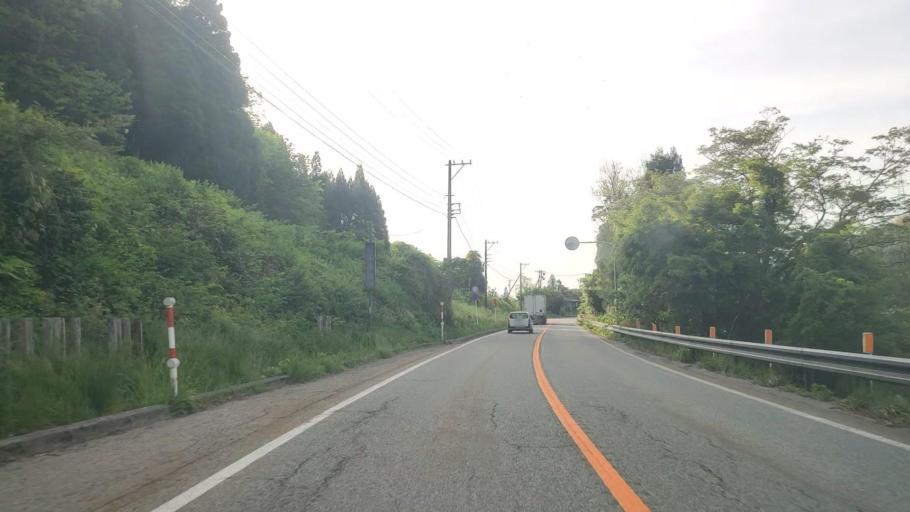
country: JP
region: Toyama
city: Yatsuomachi-higashikumisaka
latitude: 36.5534
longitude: 137.2200
